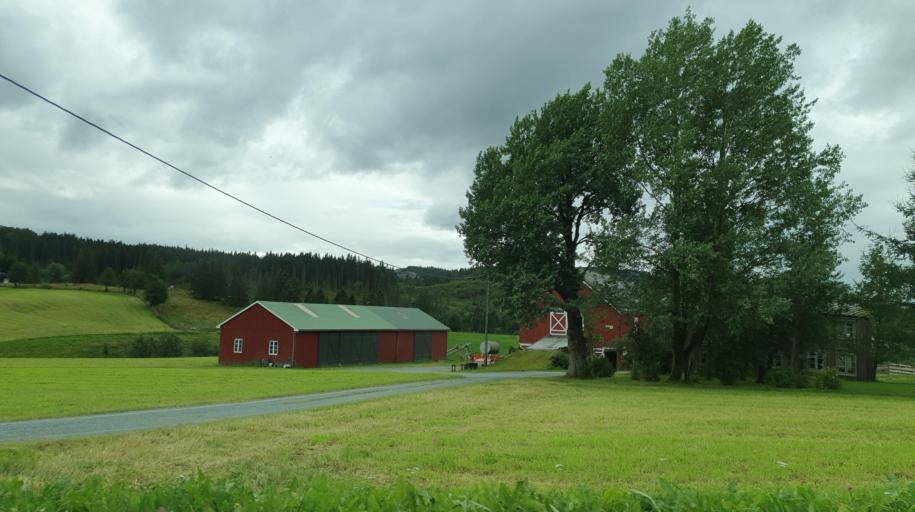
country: NO
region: Nord-Trondelag
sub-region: Stjordal
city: Stjordalshalsen
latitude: 63.4147
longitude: 10.9611
